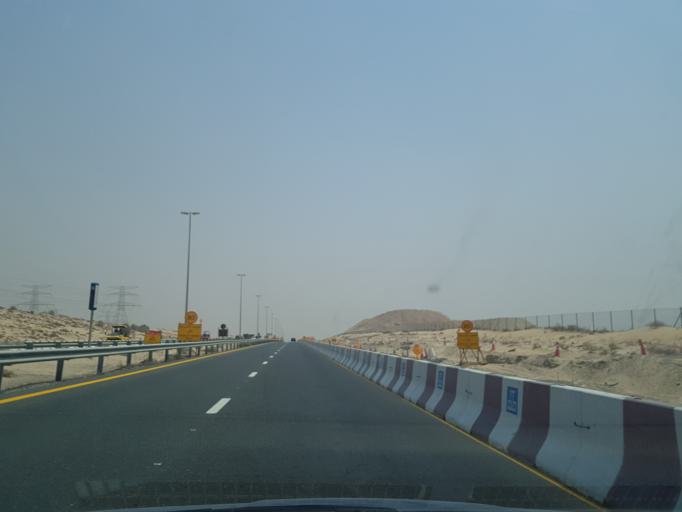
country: AE
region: Ash Shariqah
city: Sharjah
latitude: 25.1445
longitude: 55.4217
